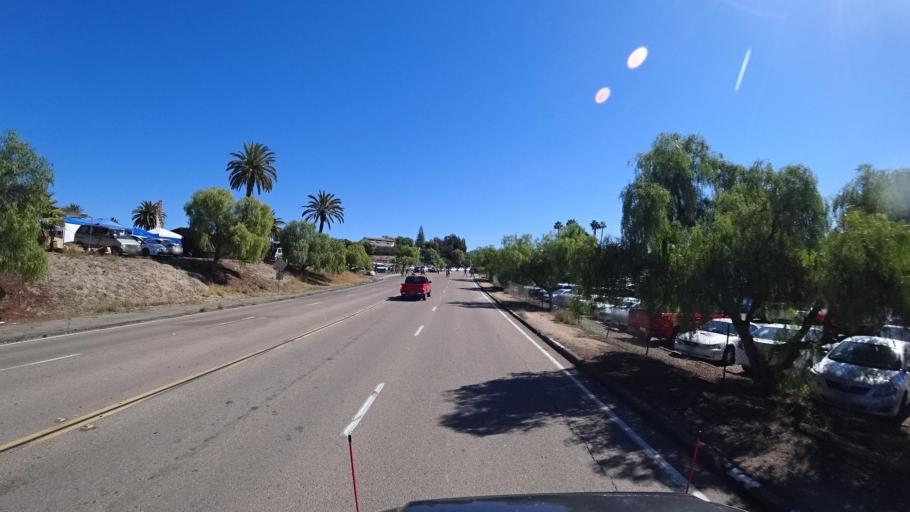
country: US
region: California
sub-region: San Diego County
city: La Presa
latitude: 32.7011
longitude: -117.0077
